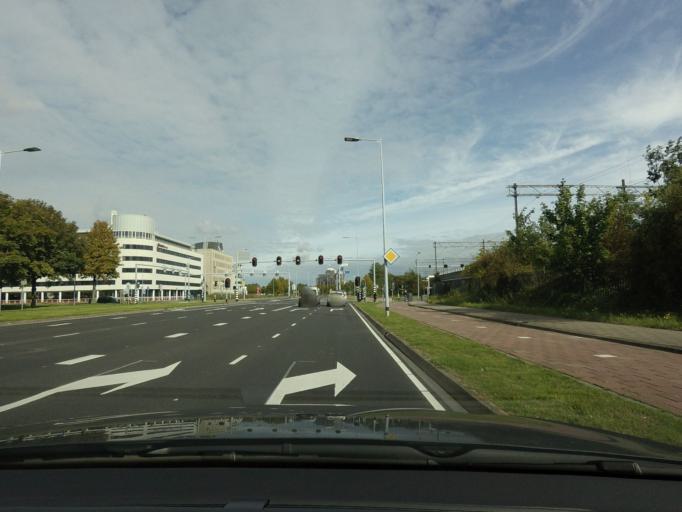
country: NL
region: North Holland
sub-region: Gemeente Haarlemmermeer
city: Hoofddorp
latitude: 52.2941
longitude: 4.7012
